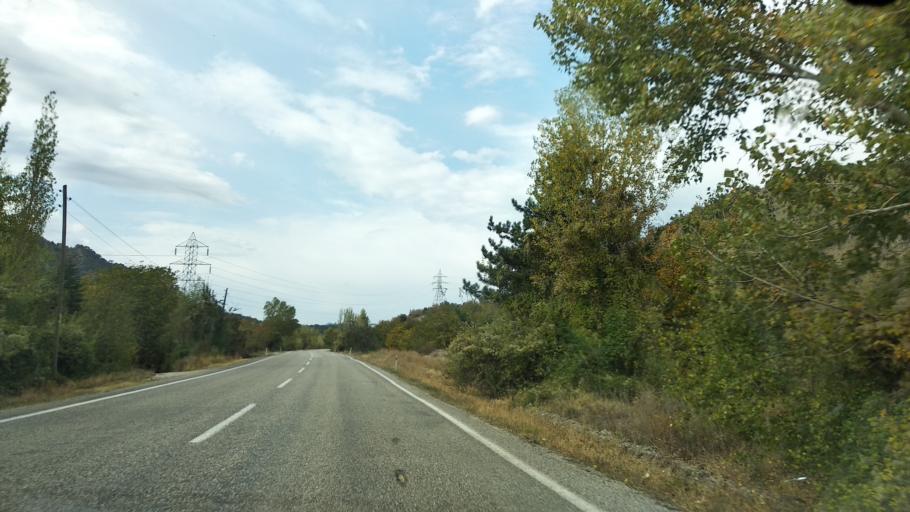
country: TR
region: Ankara
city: Nallihan
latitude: 40.3082
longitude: 31.2843
